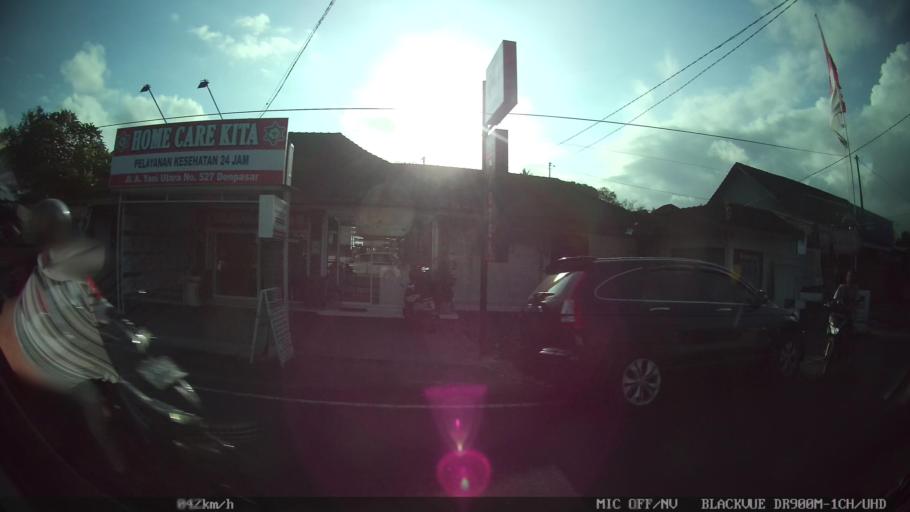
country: ID
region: Bali
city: Banjar Batur
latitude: -8.6030
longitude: 115.2140
